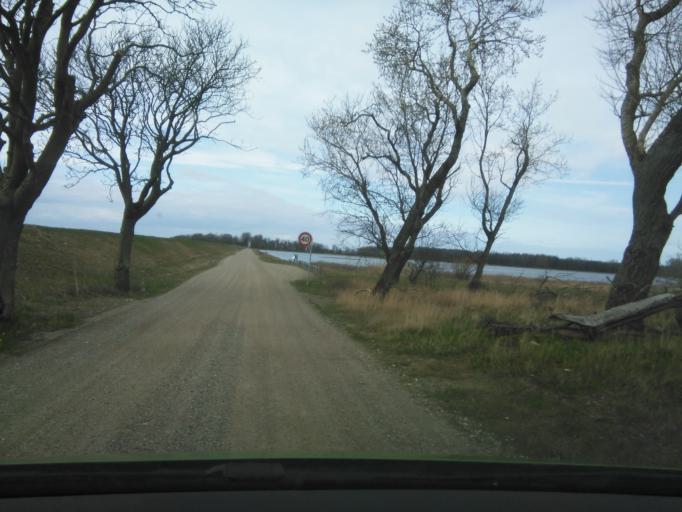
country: DK
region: South Denmark
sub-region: Nordfyns Kommune
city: Bogense
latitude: 55.5728
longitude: 10.1608
